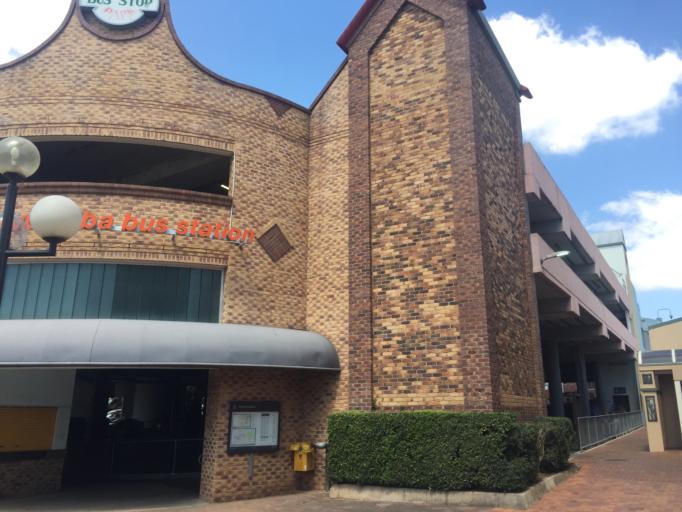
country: AU
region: Queensland
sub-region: Toowoomba
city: Toowoomba
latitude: -27.5600
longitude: 151.9550
